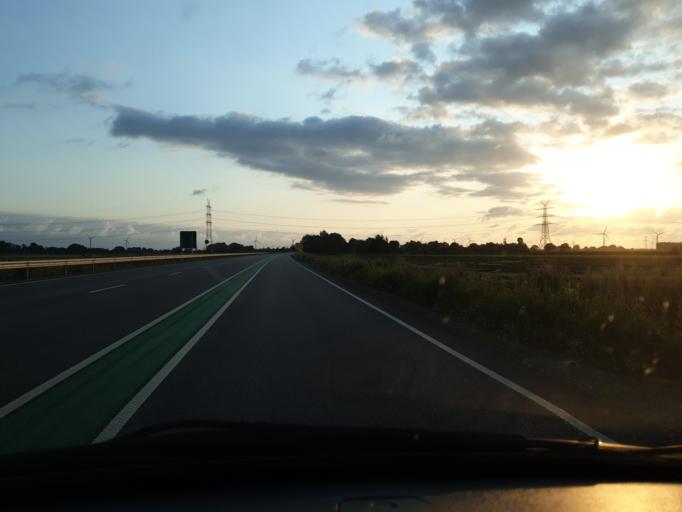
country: DE
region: Schleswig-Holstein
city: Dammfleth
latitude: 53.9113
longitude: 9.3646
